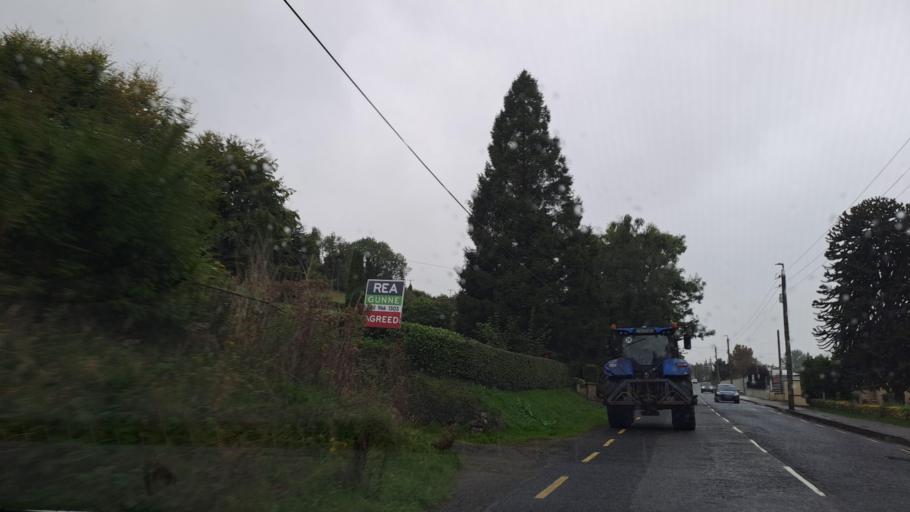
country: IE
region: Ulster
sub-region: County Monaghan
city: Carrickmacross
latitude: 53.9729
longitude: -6.7081
